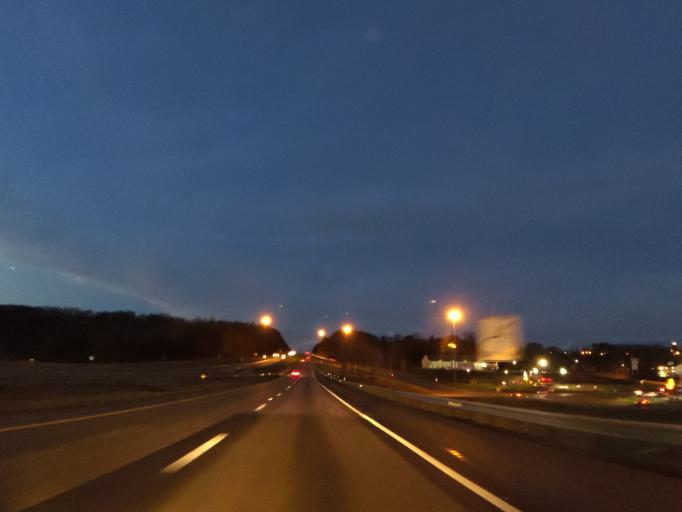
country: US
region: Kentucky
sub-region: Whitley County
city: Corbin
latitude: 36.9163
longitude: -84.1299
